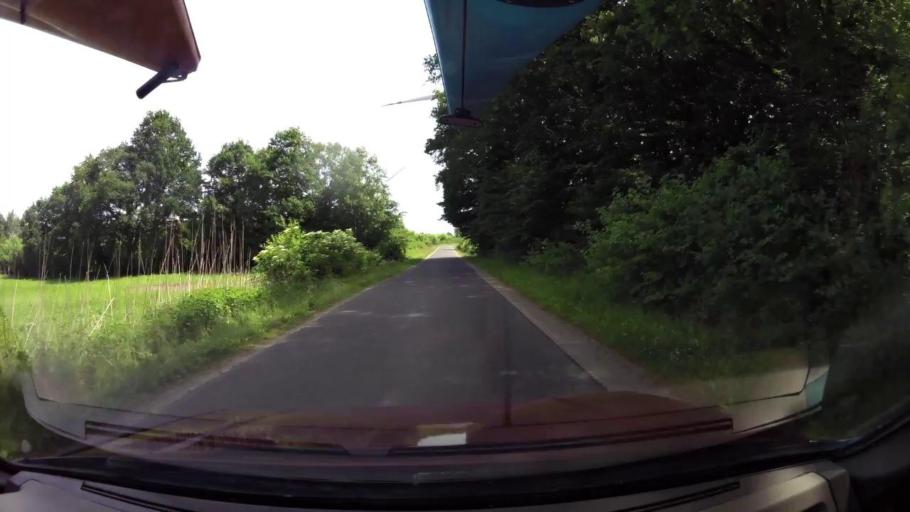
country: PL
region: West Pomeranian Voivodeship
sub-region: Powiat slawienski
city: Darlowo
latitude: 54.3124
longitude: 16.4684
